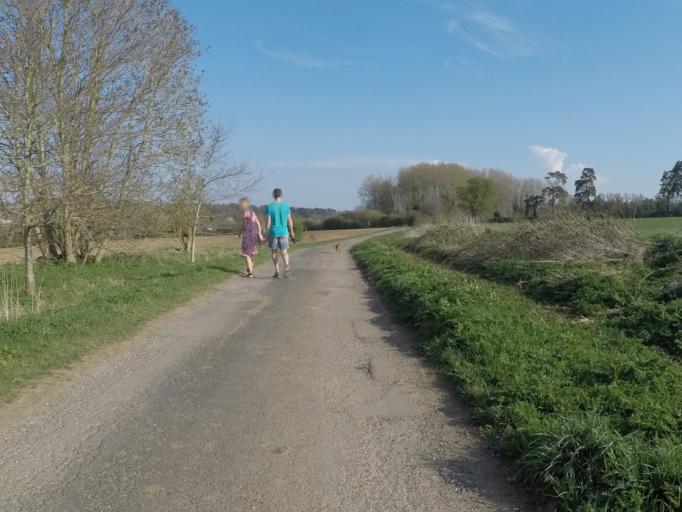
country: GB
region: England
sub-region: Oxfordshire
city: Charlbury
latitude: 51.8745
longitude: -1.4964
